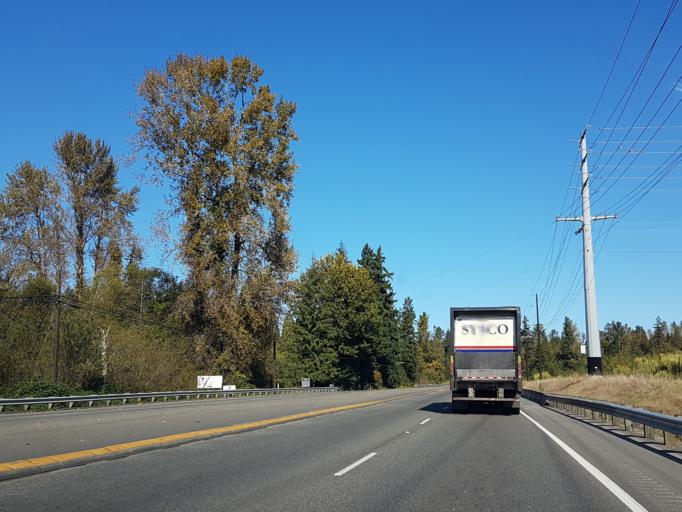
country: US
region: Washington
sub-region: Snohomish County
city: Maltby
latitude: 47.7910
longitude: -122.1432
